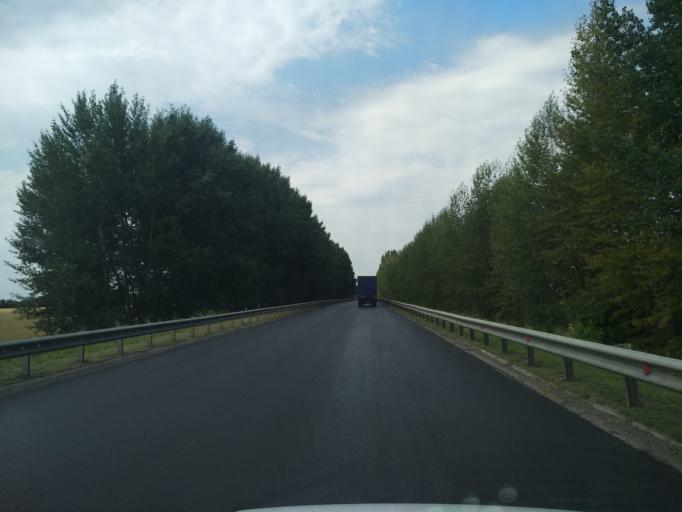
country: RU
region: Voronezj
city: Pereleshino
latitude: 51.7578
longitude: 40.1193
